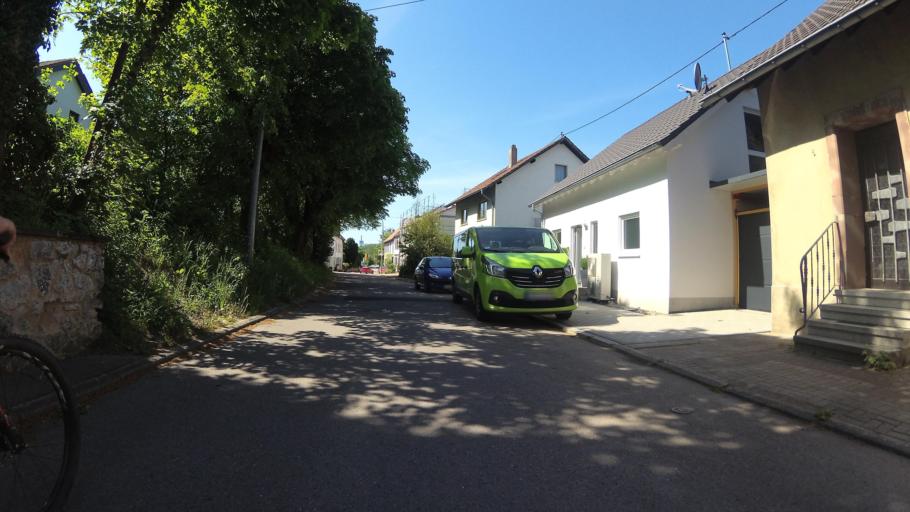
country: DE
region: Saarland
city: Gersheim
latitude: 49.1861
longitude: 7.1642
